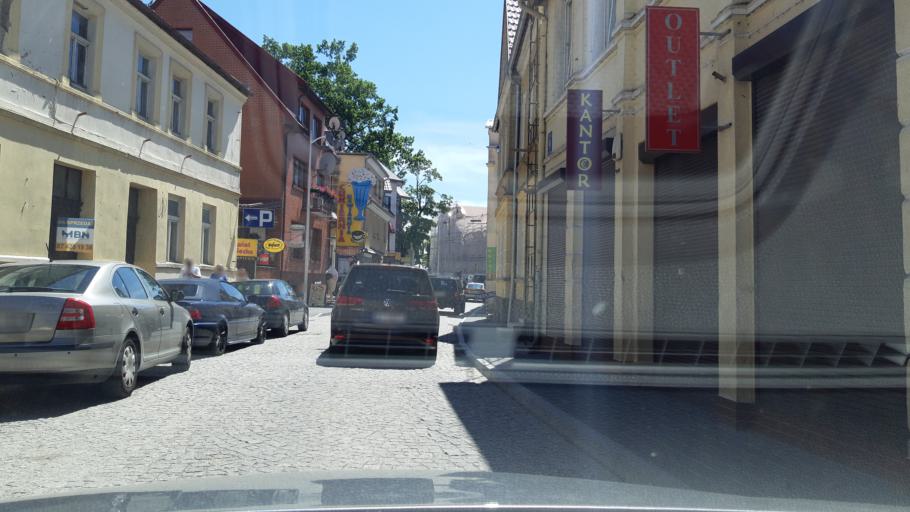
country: PL
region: Warmian-Masurian Voivodeship
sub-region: Powiat mragowski
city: Mikolajki
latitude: 53.8019
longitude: 21.5718
